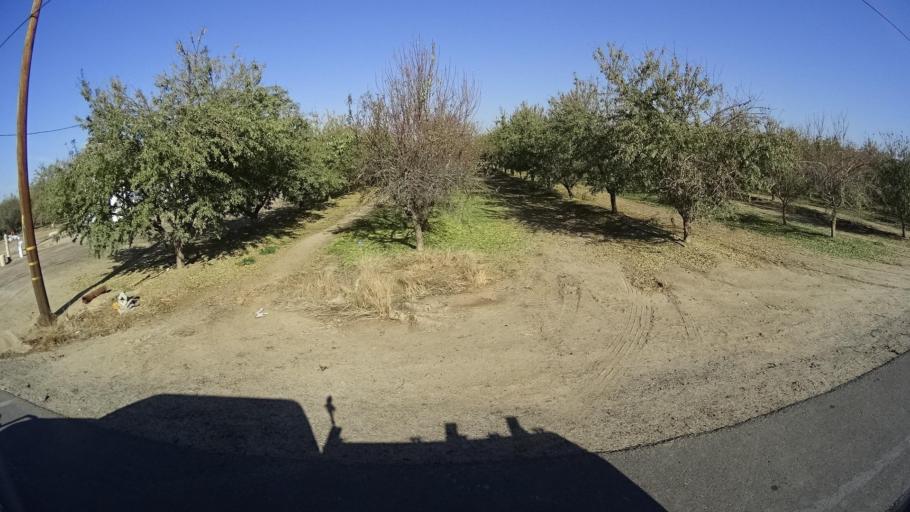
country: US
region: California
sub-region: Kern County
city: Delano
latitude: 35.7178
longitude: -119.3161
